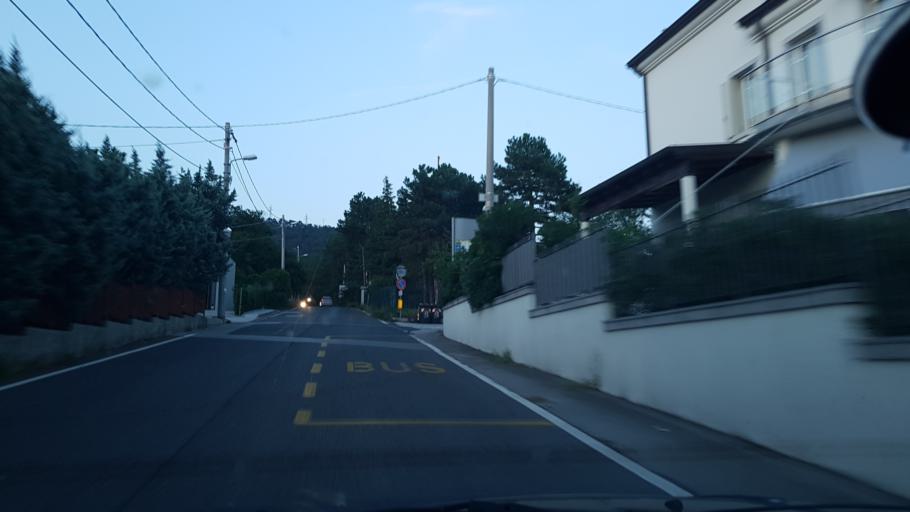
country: IT
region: Friuli Venezia Giulia
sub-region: Provincia di Trieste
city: Villa Opicina
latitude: 45.6763
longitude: 13.7680
